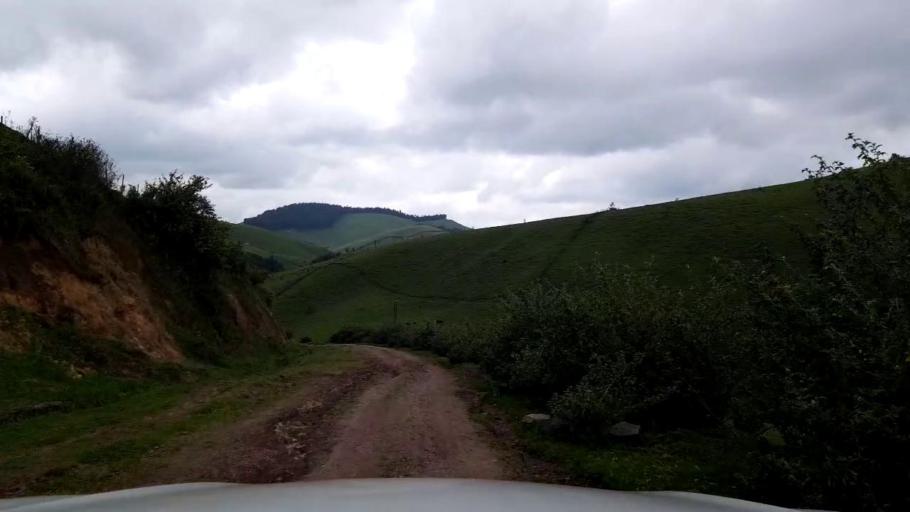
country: RW
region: Western Province
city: Gisenyi
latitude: -1.6810
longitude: 29.4174
